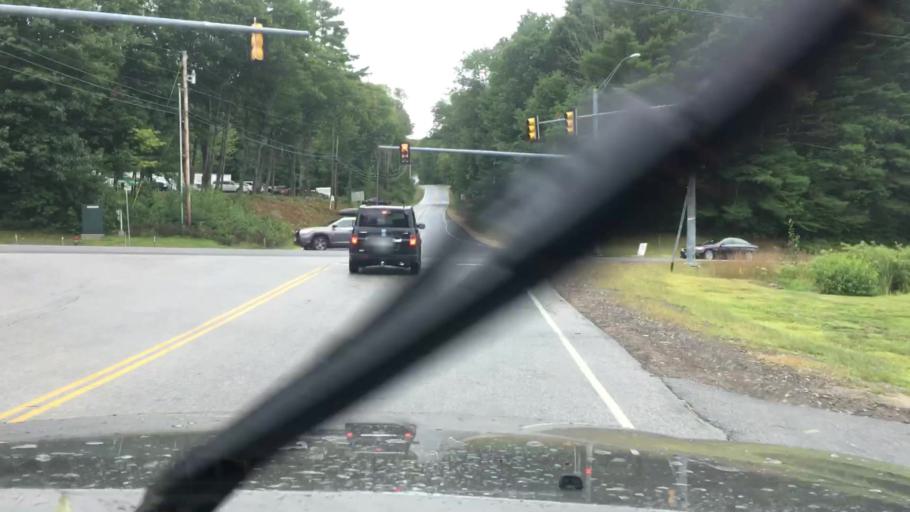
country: US
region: New Hampshire
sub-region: Belknap County
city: Meredith
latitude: 43.6392
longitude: -71.5301
